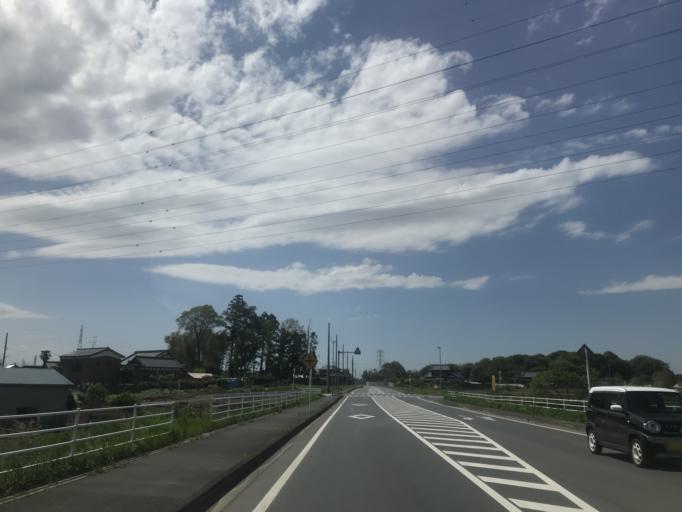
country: JP
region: Chiba
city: Noda
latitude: 35.9642
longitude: 139.9031
